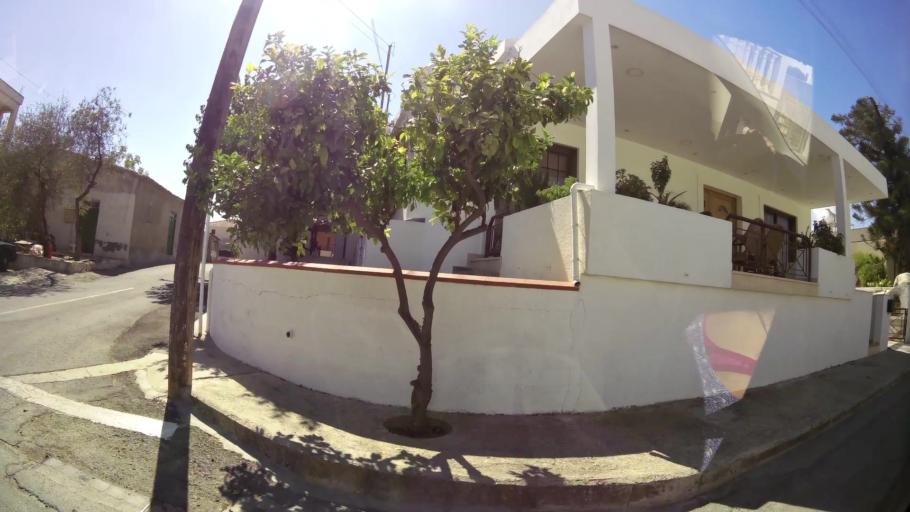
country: CY
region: Larnaka
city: Livadia
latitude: 34.9548
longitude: 33.6277
